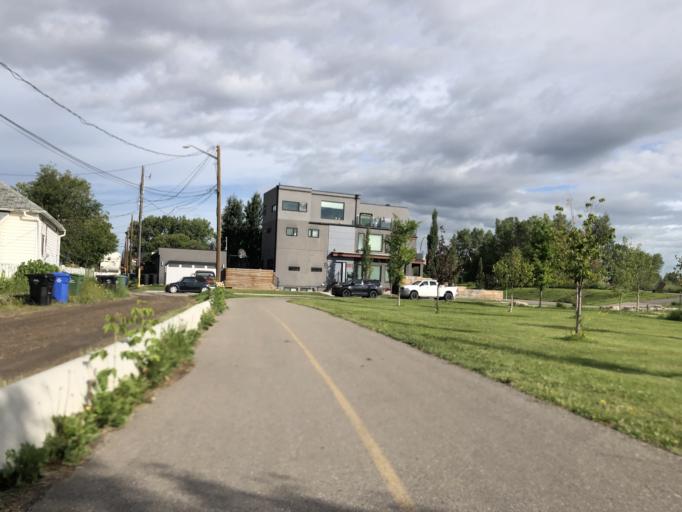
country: CA
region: Alberta
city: Calgary
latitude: 51.0344
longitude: -114.0142
